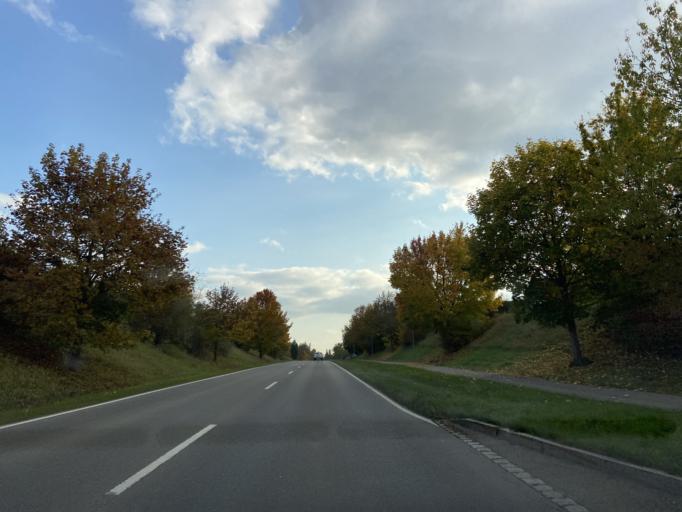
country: DE
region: Baden-Wuerttemberg
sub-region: Tuebingen Region
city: Sigmaringen
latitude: 48.0927
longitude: 9.2408
